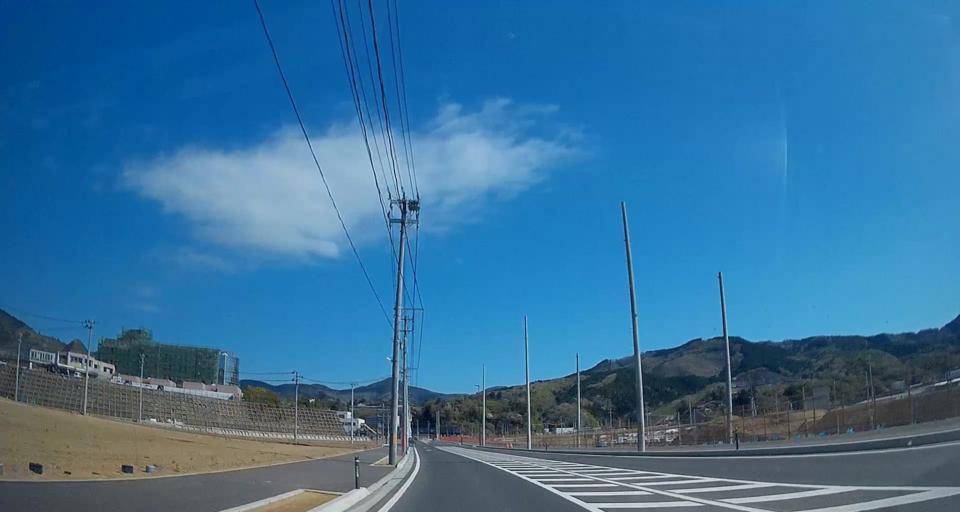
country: JP
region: Miyagi
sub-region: Oshika Gun
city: Onagawa Cho
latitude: 38.4419
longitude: 141.4467
